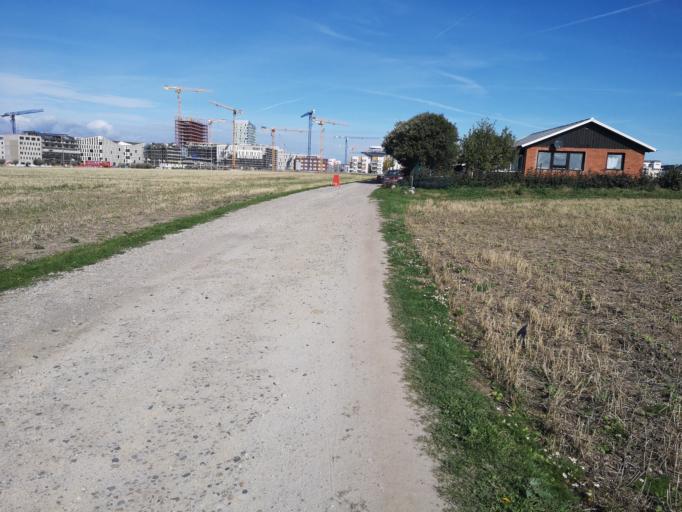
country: SE
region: Skane
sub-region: Malmo
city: Bunkeflostrand
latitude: 55.5565
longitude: 12.9785
